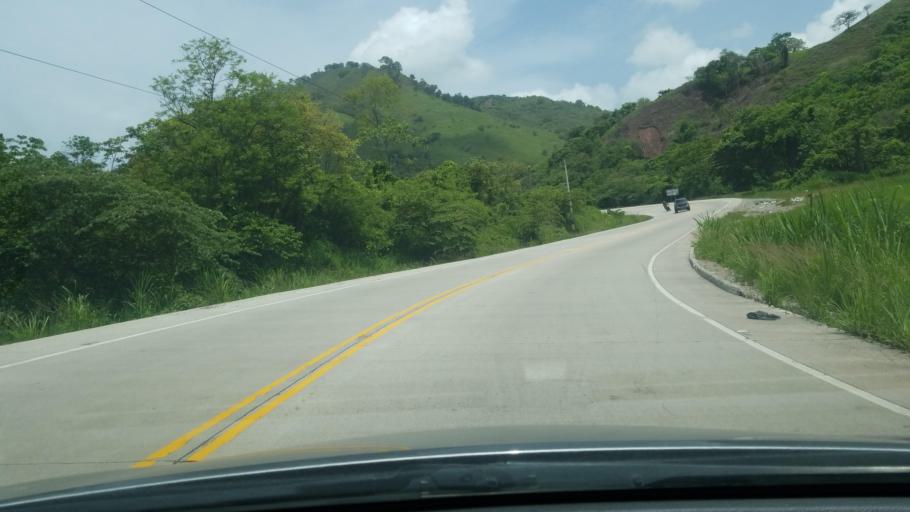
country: HN
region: Copan
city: Veracruz
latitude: 14.8795
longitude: -88.7772
